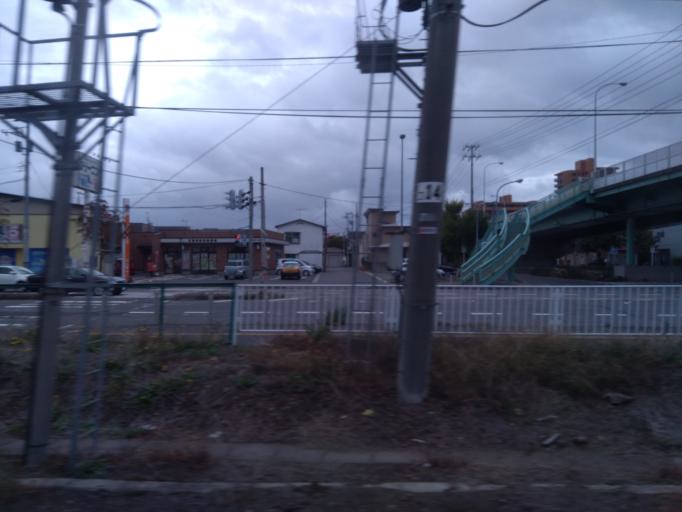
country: JP
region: Hokkaido
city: Hakodate
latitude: 41.8009
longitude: 140.7341
